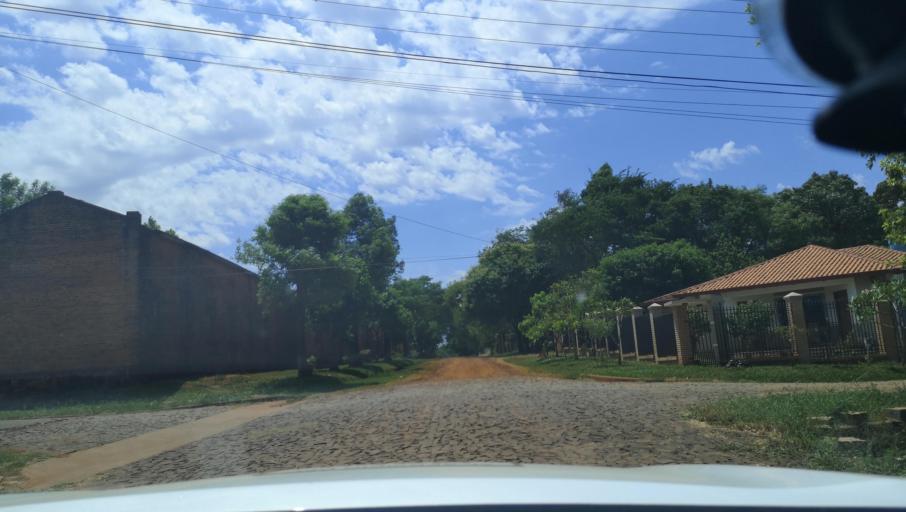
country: PY
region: Itapua
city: Carmen del Parana
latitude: -27.1645
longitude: -56.2377
